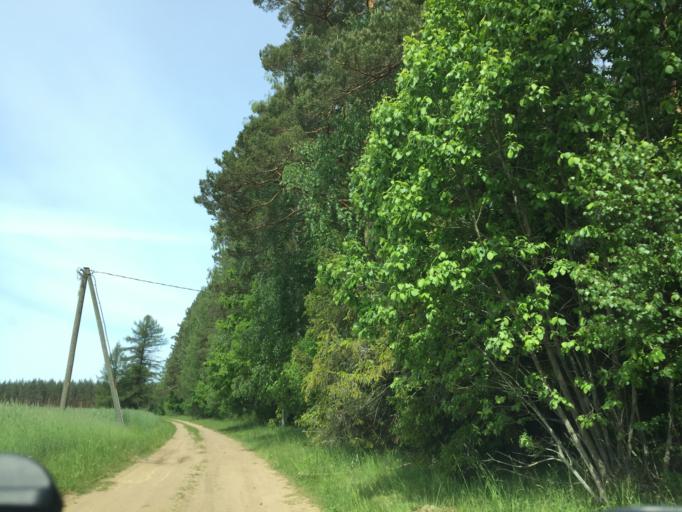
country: LV
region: Koceni
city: Koceni
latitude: 57.4434
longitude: 25.2825
